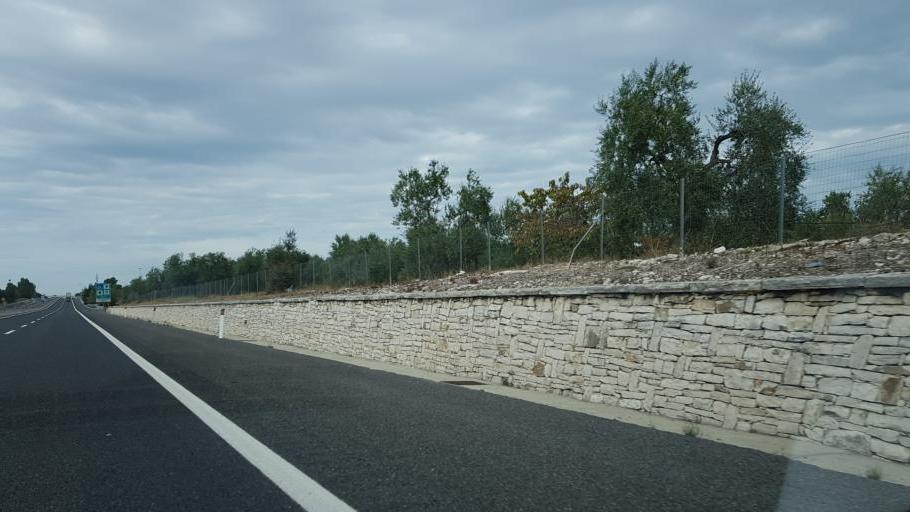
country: IT
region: Apulia
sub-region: Provincia di Barletta - Andria - Trani
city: Bisceglie
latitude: 41.1917
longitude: 16.4912
